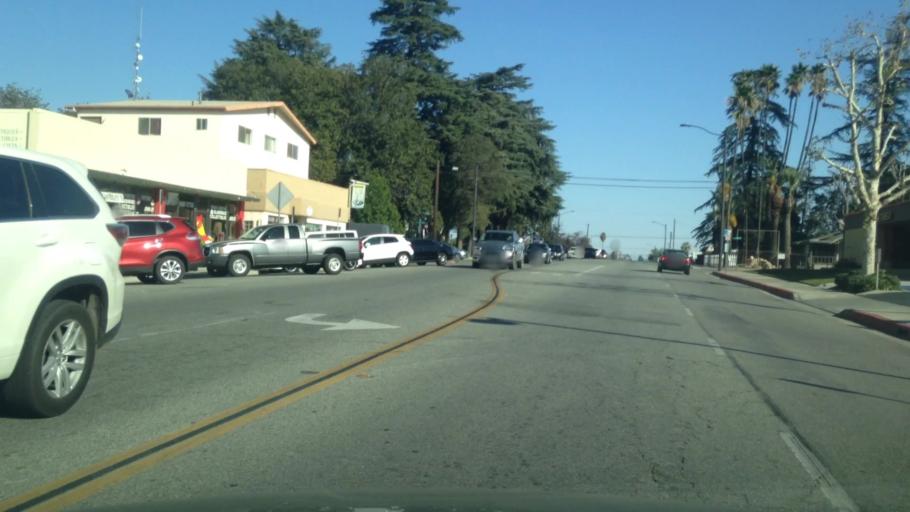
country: US
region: California
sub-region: Riverside County
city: Beaumont
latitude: 33.9293
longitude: -116.9767
